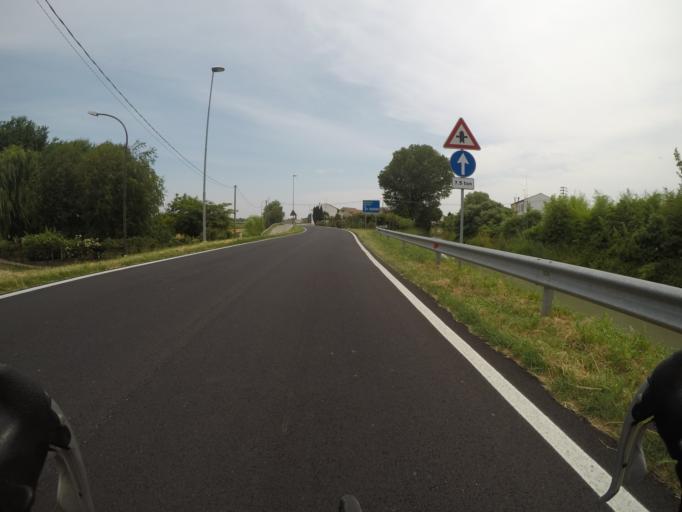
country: IT
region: Veneto
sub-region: Provincia di Rovigo
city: Costa di Rovigo
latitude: 45.0486
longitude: 11.6869
